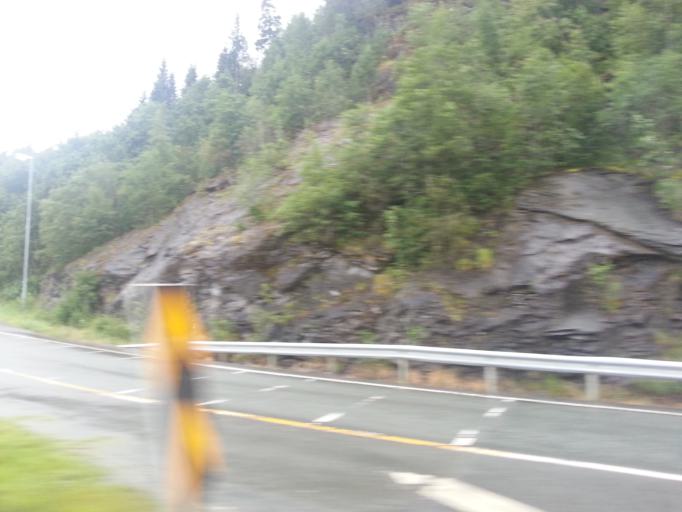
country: NO
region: Sor-Trondelag
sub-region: Malvik
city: Malvik
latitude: 63.4269
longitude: 10.6631
